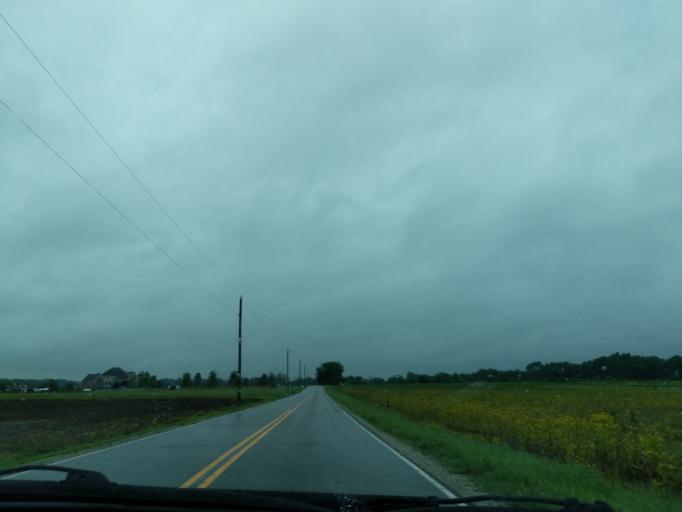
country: US
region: Indiana
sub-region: Madison County
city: Lapel
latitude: 40.0663
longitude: -85.9213
